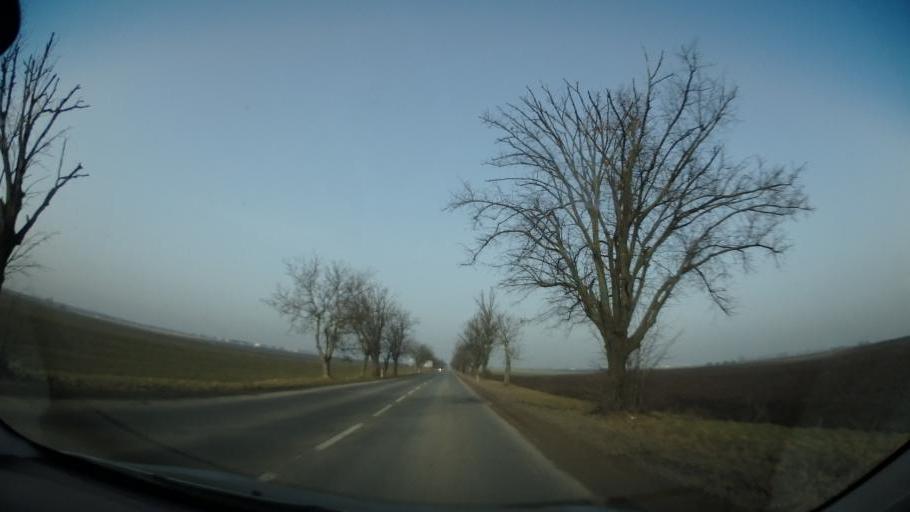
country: CZ
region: South Moravian
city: Rajhrad
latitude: 49.0692
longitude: 16.5742
